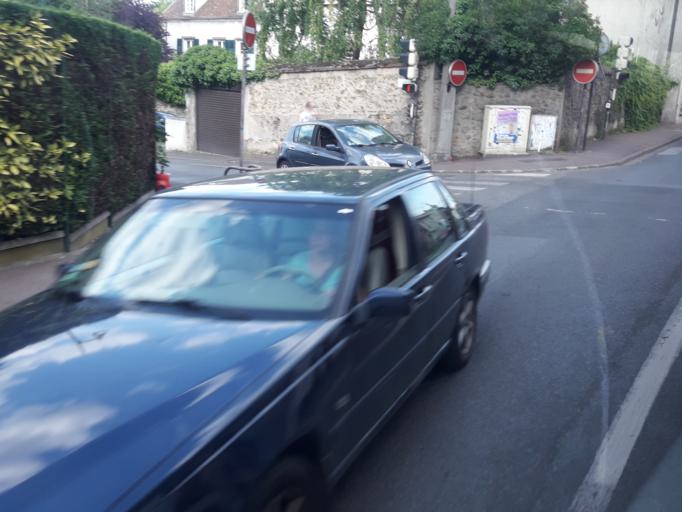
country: FR
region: Ile-de-France
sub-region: Departement de l'Essonne
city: Longjumeau
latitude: 48.6936
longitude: 2.2912
